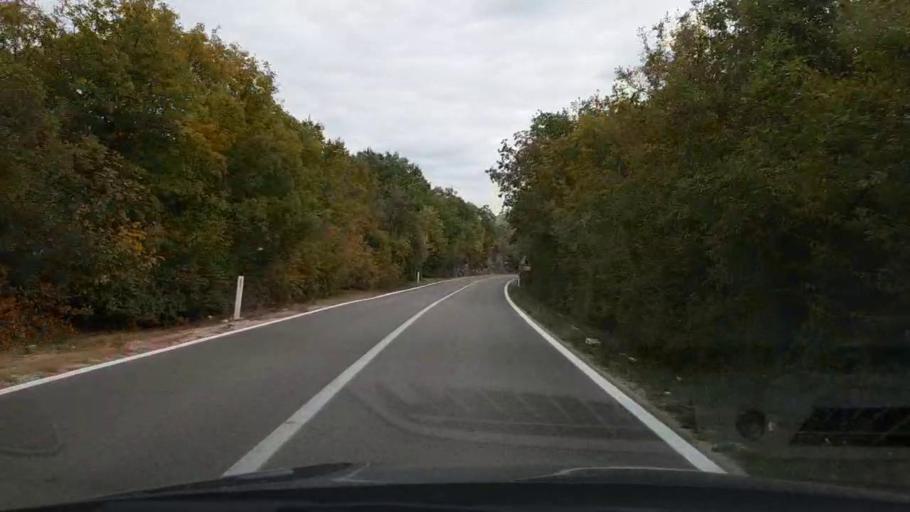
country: BA
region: Republika Srpska
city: Trebinje
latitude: 42.6871
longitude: 18.2844
